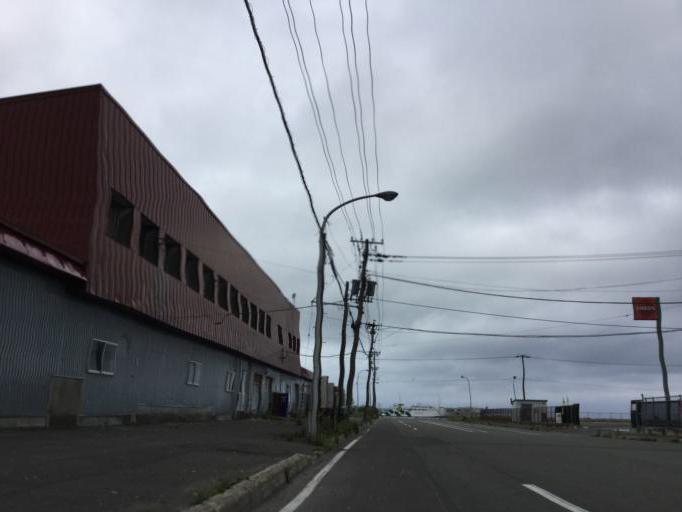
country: JP
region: Hokkaido
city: Wakkanai
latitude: 45.4082
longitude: 141.6822
